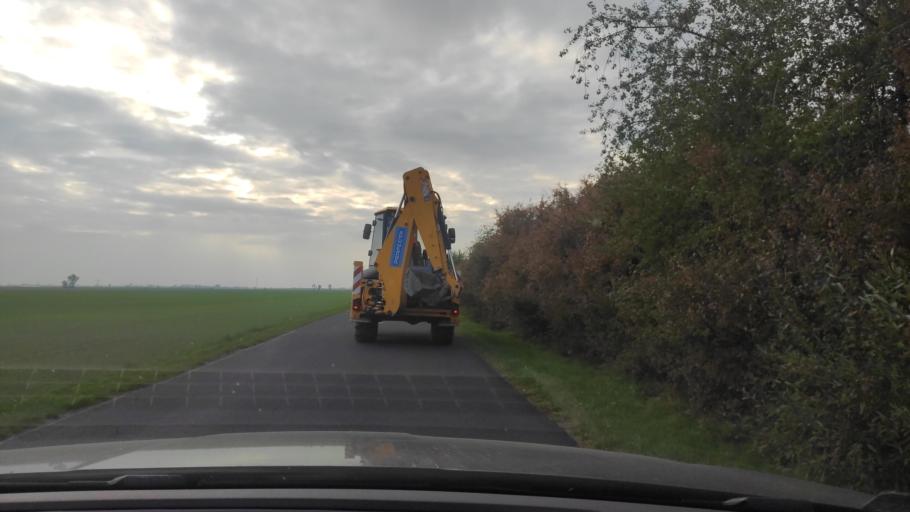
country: PL
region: Greater Poland Voivodeship
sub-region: Powiat poznanski
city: Kostrzyn
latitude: 52.4447
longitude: 17.2012
